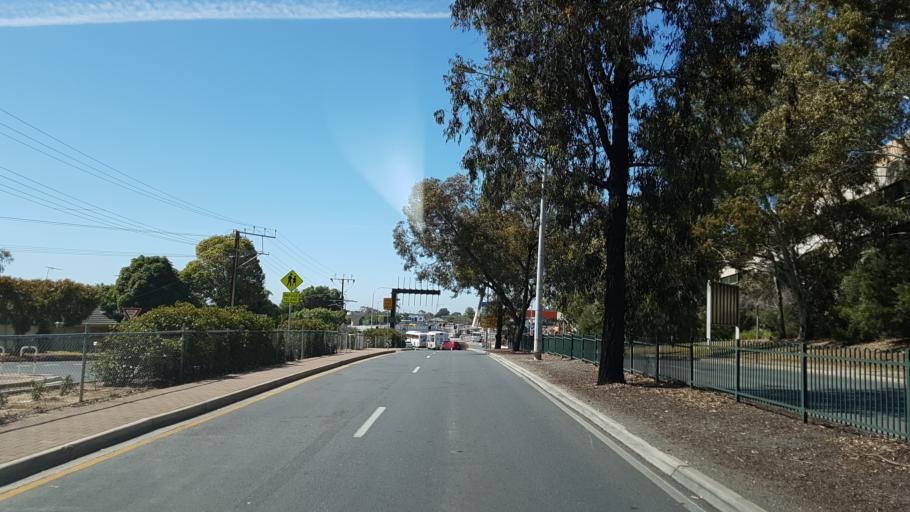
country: AU
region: South Australia
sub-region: Marion
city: Marion
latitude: -35.0210
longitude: 138.5676
